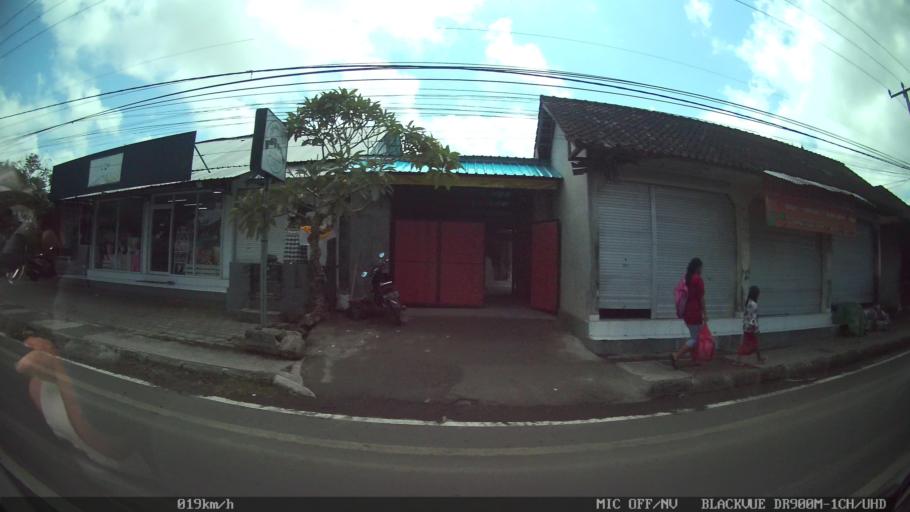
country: ID
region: Bali
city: Banjar Pasekan
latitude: -8.5938
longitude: 115.2817
